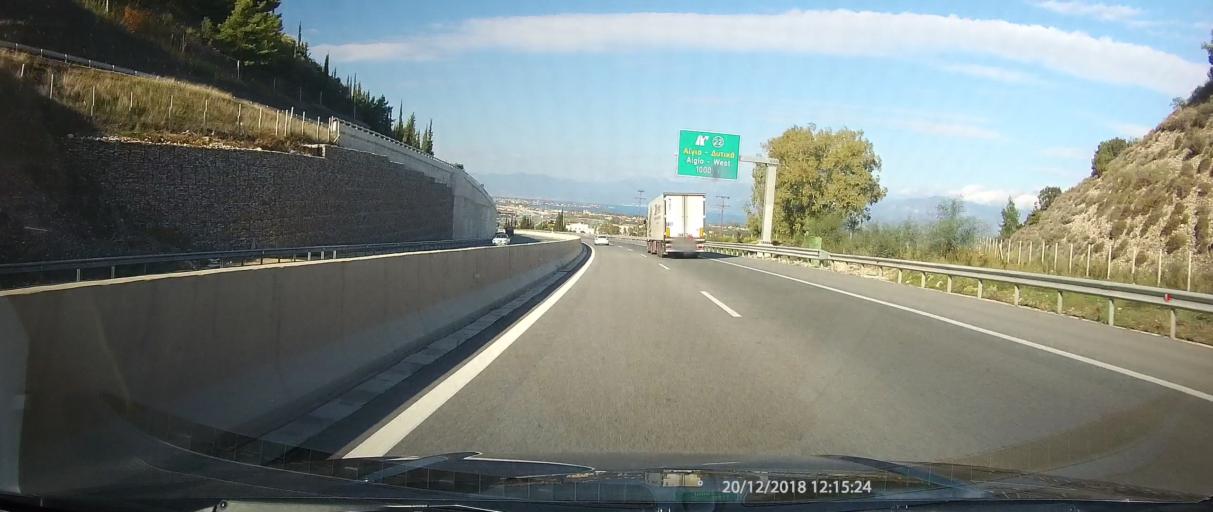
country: GR
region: West Greece
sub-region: Nomos Achaias
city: Aigio
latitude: 38.2534
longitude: 22.0690
